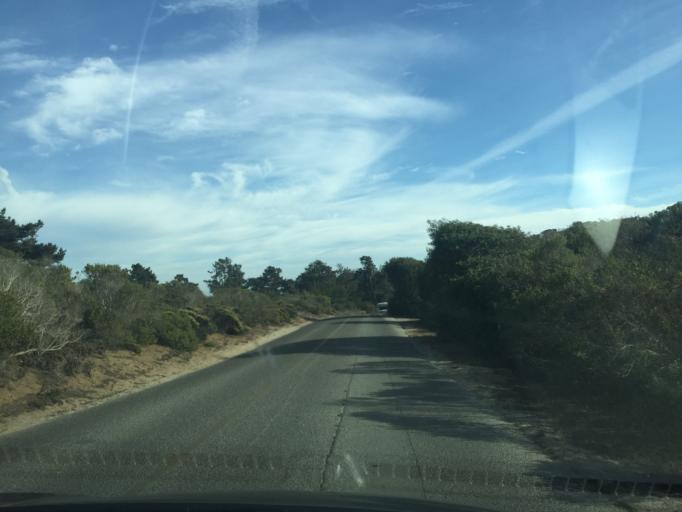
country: US
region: California
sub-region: Santa Cruz County
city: La Selva Beach
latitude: 36.8926
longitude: -121.8329
